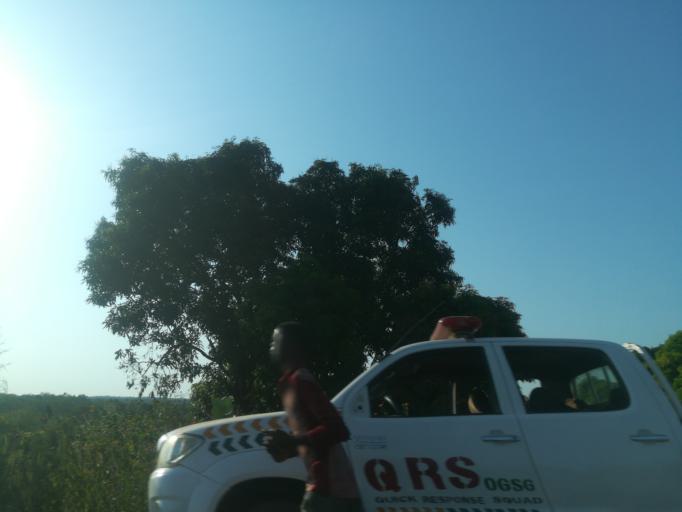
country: NG
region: Ogun
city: Abeokuta
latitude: 7.2112
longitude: 3.2932
